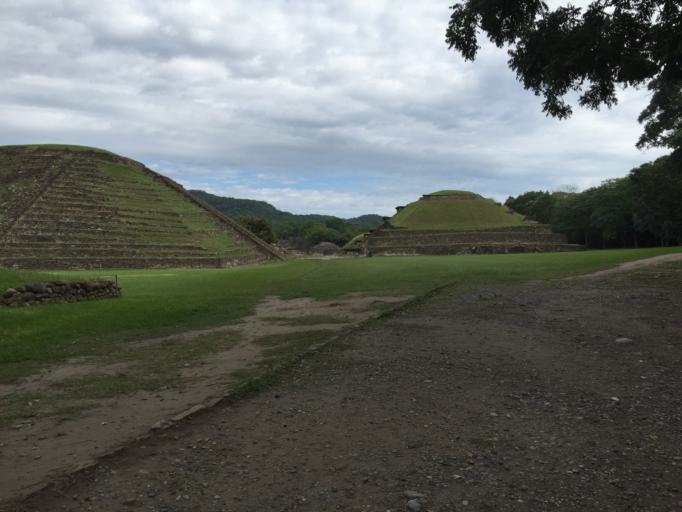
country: MX
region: Veracruz
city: Papantla de Olarte
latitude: 20.4445
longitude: -97.3776
